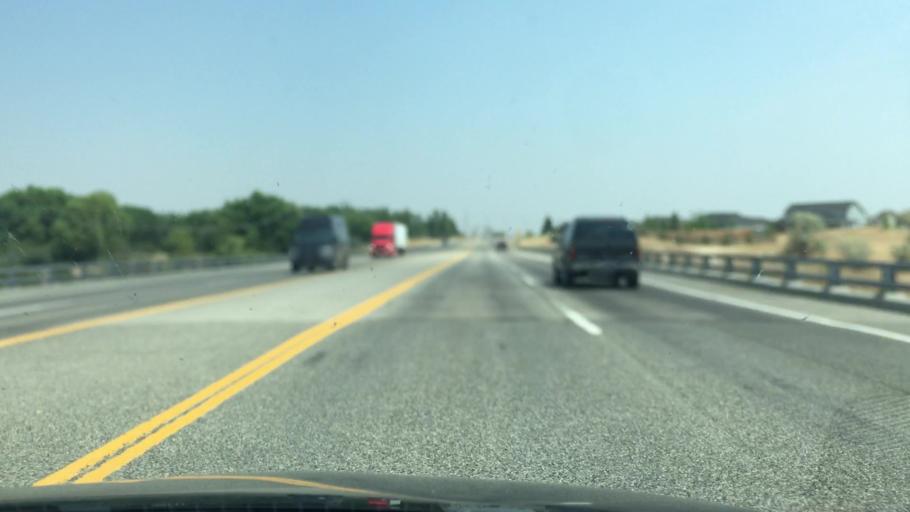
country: US
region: Idaho
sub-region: Twin Falls County
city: Twin Falls
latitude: 42.5934
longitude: -114.5306
